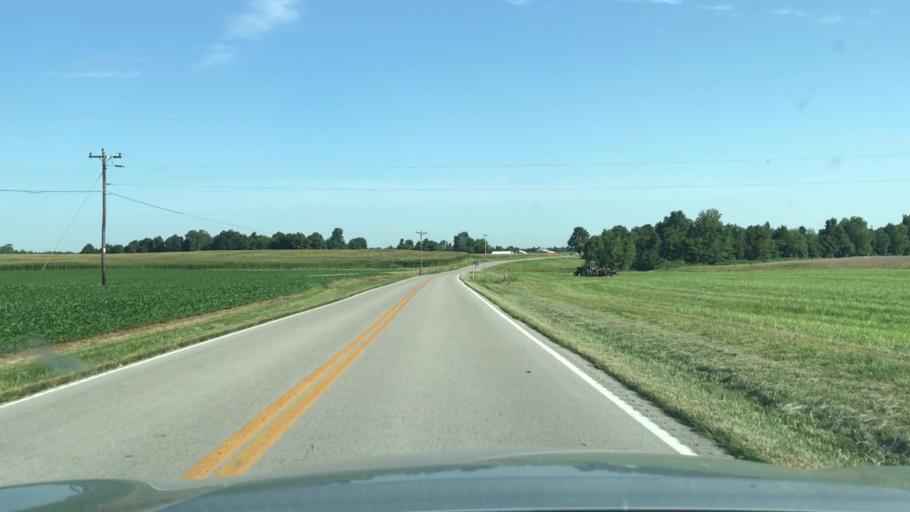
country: US
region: Kentucky
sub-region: Muhlenberg County
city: Greenville
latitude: 37.0174
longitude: -87.1321
